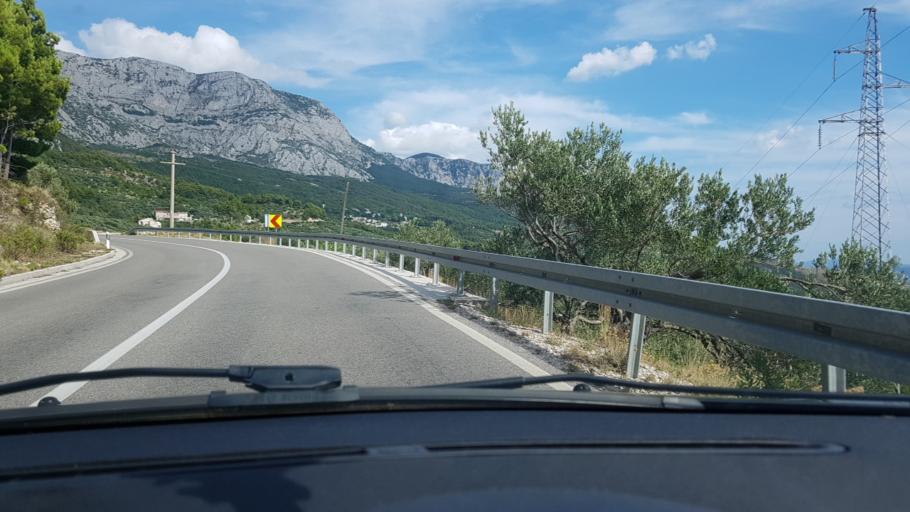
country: HR
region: Splitsko-Dalmatinska
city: Tucepi
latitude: 43.2787
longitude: 17.0542
